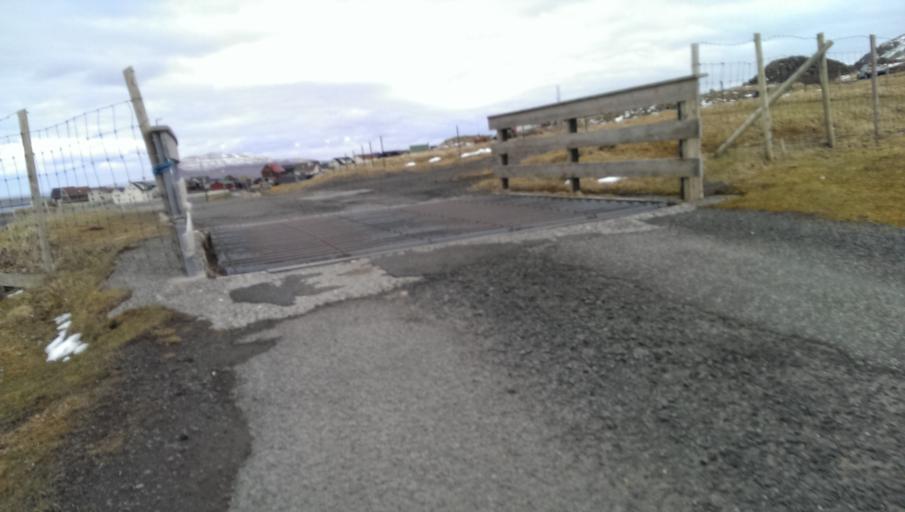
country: FO
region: Streymoy
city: Hoyvik
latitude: 62.0322
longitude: -6.7997
